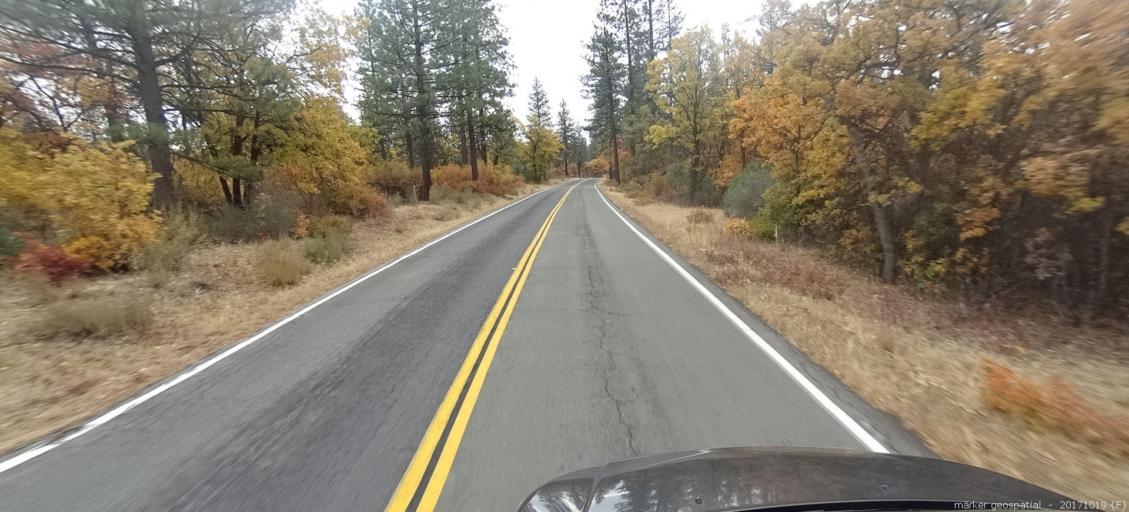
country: US
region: California
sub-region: Shasta County
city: Burney
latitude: 41.1459
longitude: -121.3491
